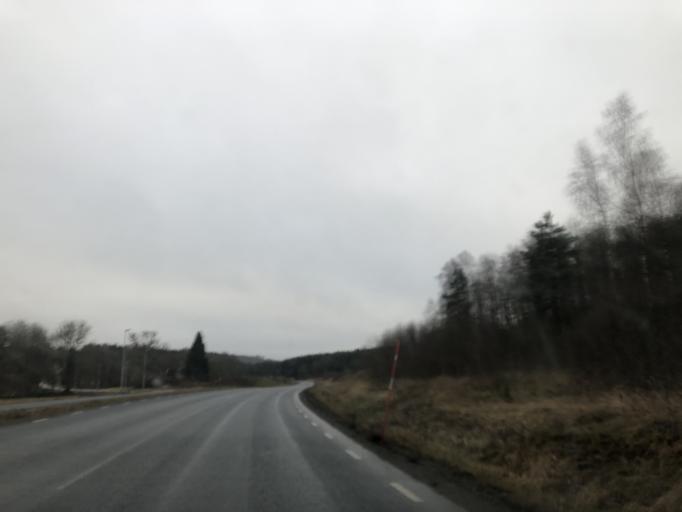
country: SE
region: Vaestra Goetaland
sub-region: Ulricehamns Kommun
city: Ulricehamn
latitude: 57.8269
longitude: 13.2895
